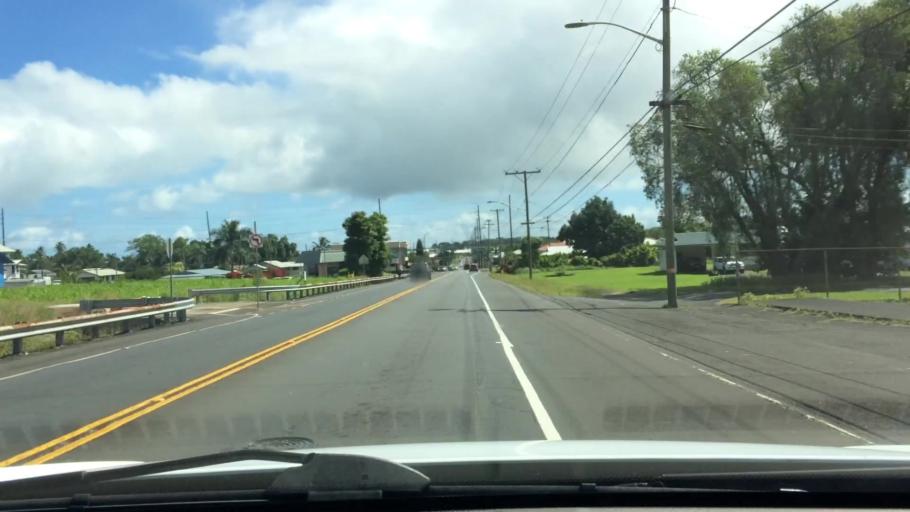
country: US
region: Hawaii
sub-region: Hawaii County
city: Hilo
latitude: 19.7016
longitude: -155.0762
